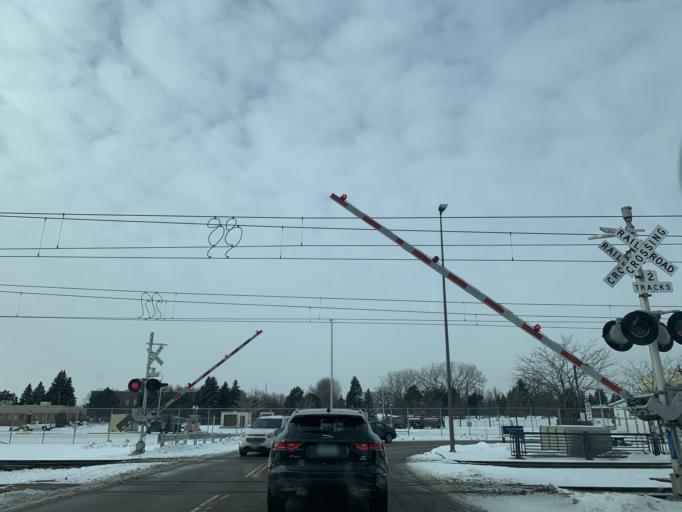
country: US
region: Minnesota
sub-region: Dakota County
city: Mendota Heights
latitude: 44.8927
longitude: -93.1981
